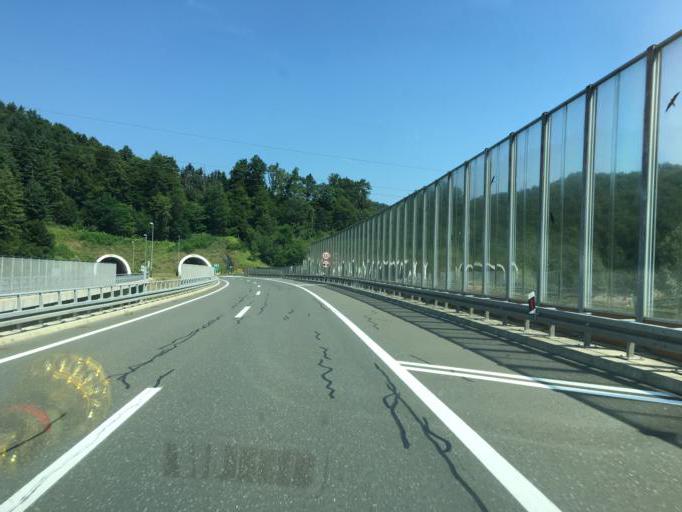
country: HR
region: Krapinsko-Zagorska
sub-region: Grad Krapina
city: Krapina
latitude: 46.2078
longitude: 15.8463
